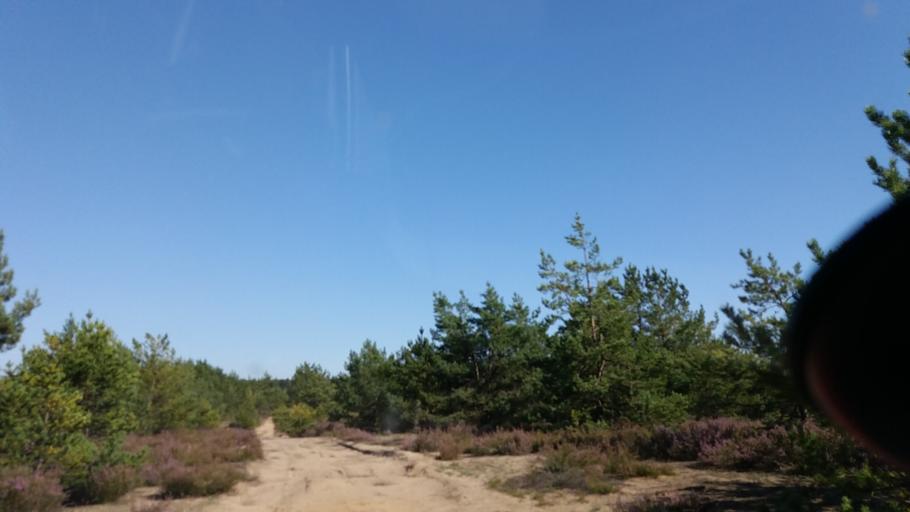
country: PL
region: West Pomeranian Voivodeship
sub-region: Powiat szczecinecki
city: Borne Sulinowo
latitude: 53.5823
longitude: 16.5001
